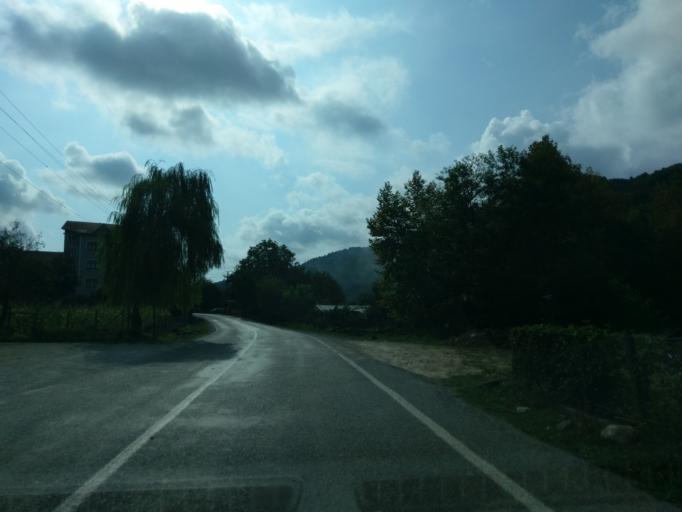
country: TR
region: Sinop
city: Helaldi
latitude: 41.9044
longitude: 34.4458
